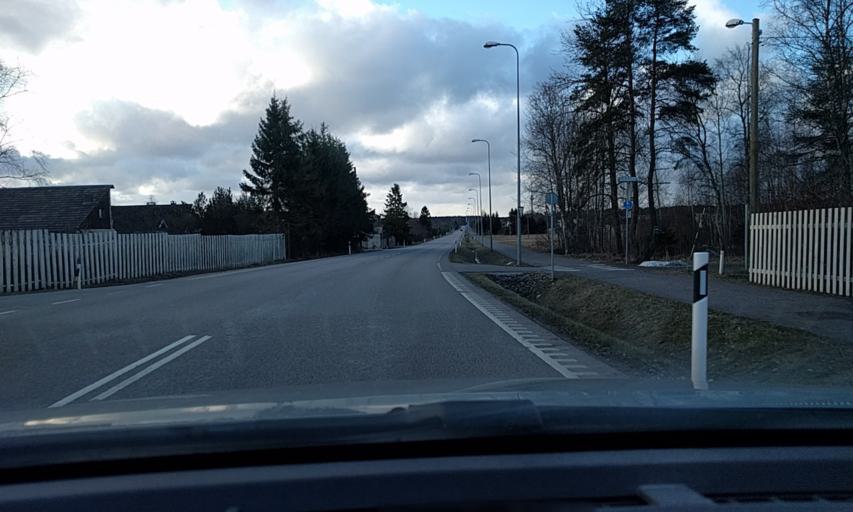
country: EE
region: Harju
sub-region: Viimsi vald
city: Viimsi
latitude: 59.5115
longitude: 24.9068
